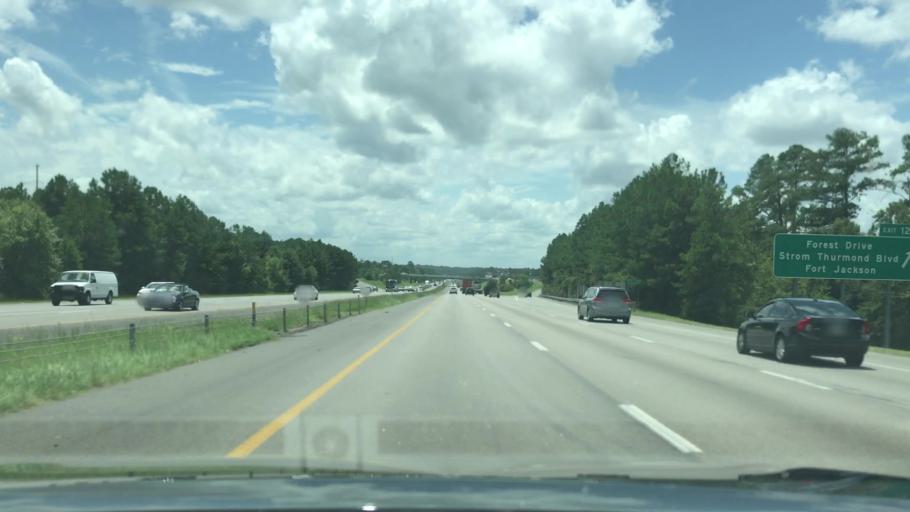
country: US
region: South Carolina
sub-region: Richland County
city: Woodfield
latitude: 34.0276
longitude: -80.9397
